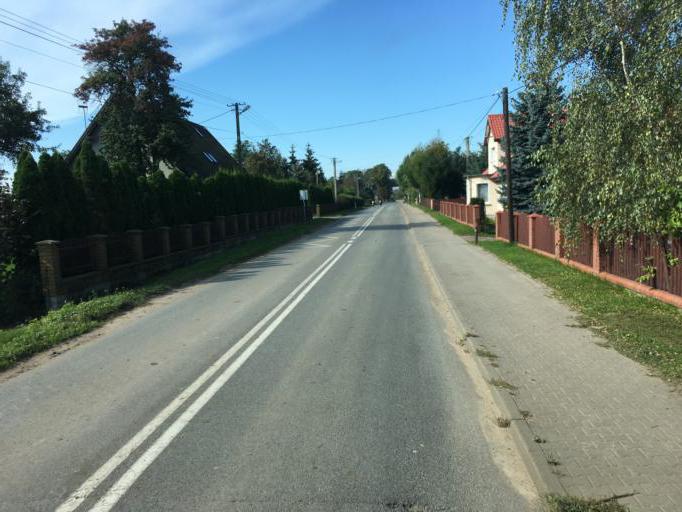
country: PL
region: Kujawsko-Pomorskie
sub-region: Powiat swiecki
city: Lniano
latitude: 53.5060
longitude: 18.1684
